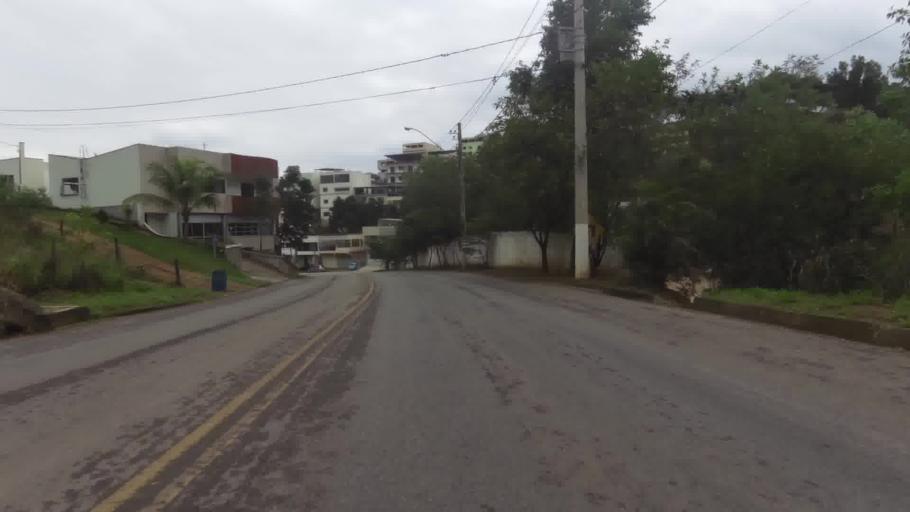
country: BR
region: Espirito Santo
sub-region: Iconha
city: Iconha
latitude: -20.7864
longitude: -40.8157
